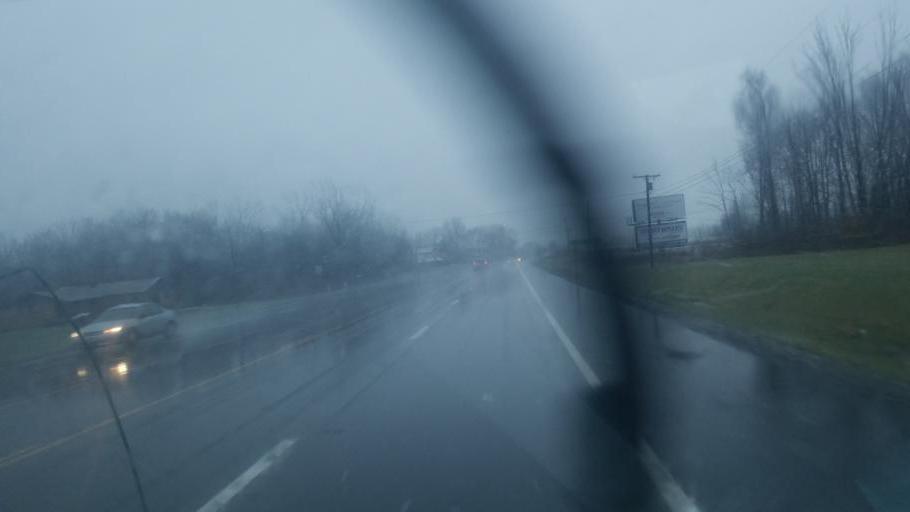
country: US
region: Ohio
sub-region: Richland County
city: Shelby
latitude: 40.8422
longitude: -82.6124
